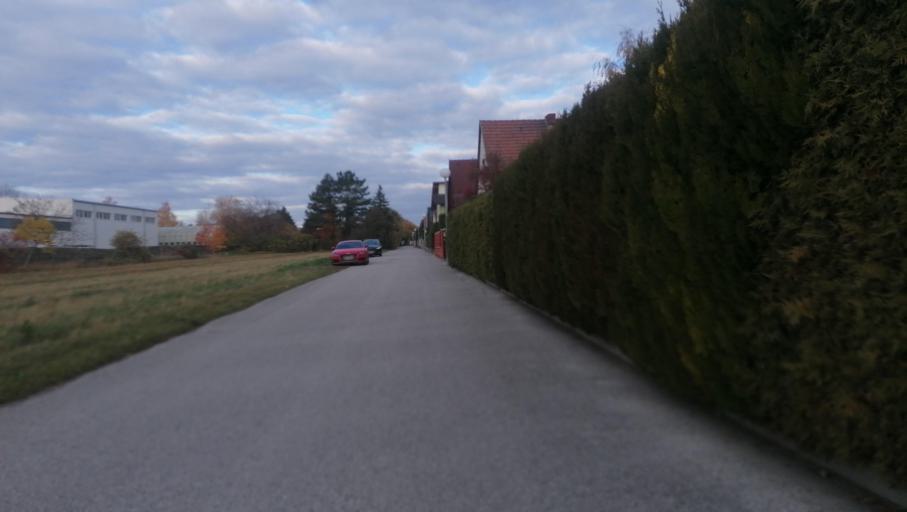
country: AT
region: Lower Austria
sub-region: Politischer Bezirk Baden
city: Oberwaltersdorf
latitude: 47.9760
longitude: 16.3275
